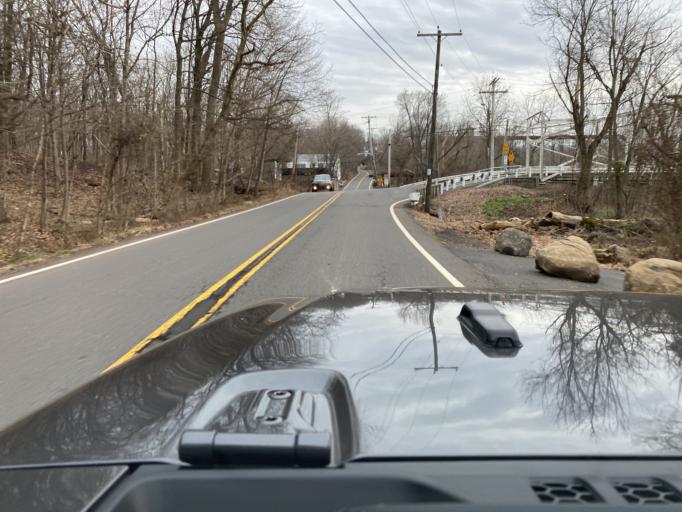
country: US
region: New Jersey
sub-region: Somerset County
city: Bloomingdale
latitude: 40.5101
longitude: -74.7267
